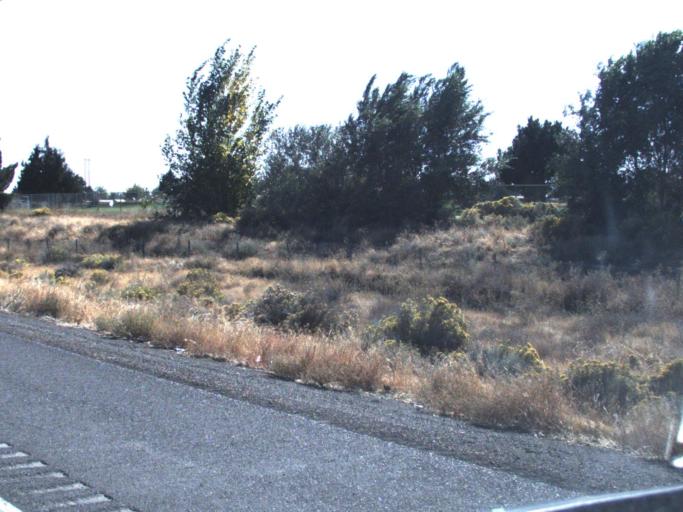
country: US
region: Washington
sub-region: Franklin County
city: Pasco
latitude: 46.2472
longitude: -119.0684
